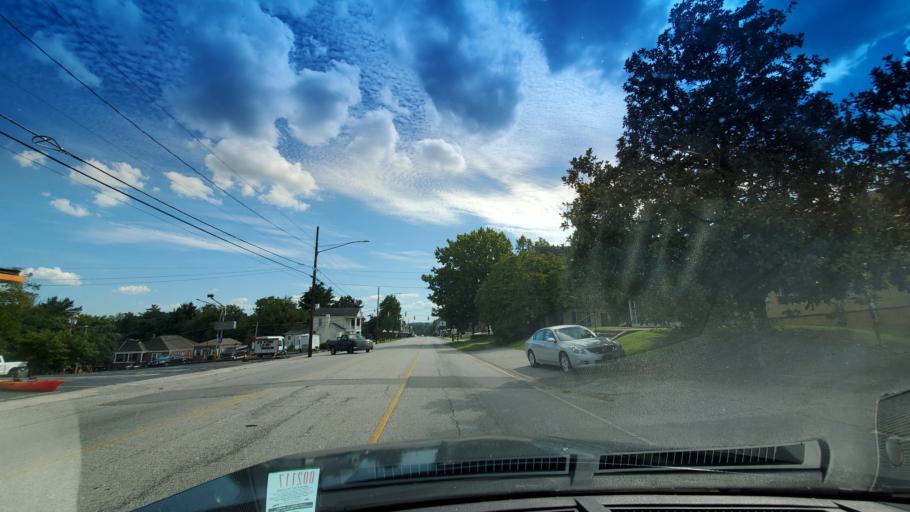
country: US
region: Tennessee
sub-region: Smith County
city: Carthage
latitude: 36.2546
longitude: -85.9517
